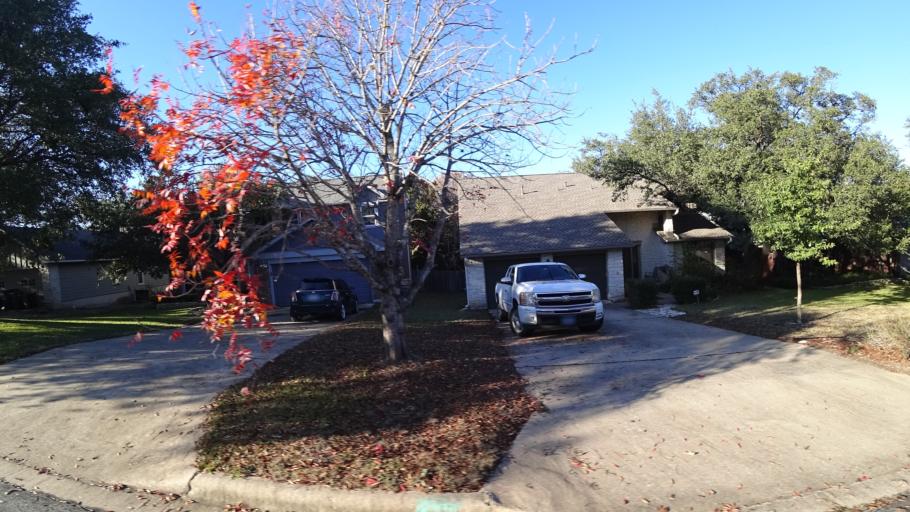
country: US
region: Texas
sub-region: Travis County
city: Wells Branch
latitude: 30.3995
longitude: -97.6975
